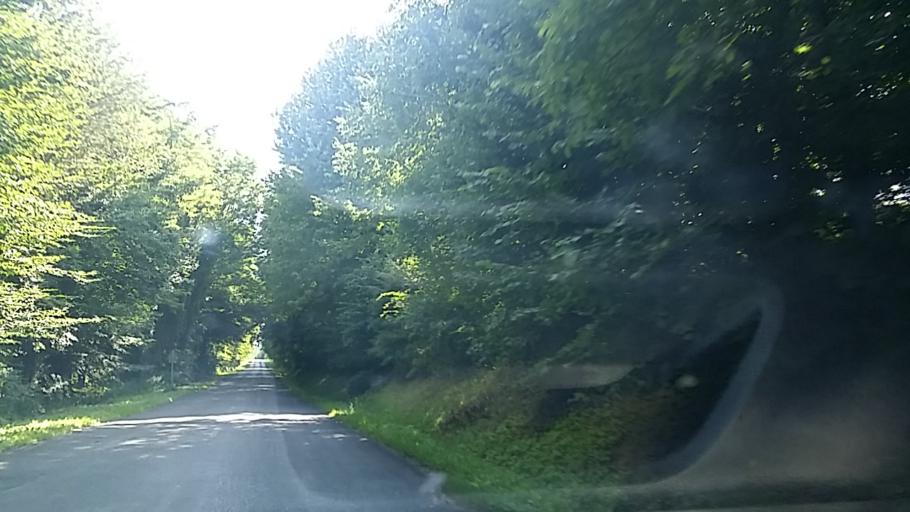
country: HU
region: Zala
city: Becsehely
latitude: 46.5286
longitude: 16.7489
